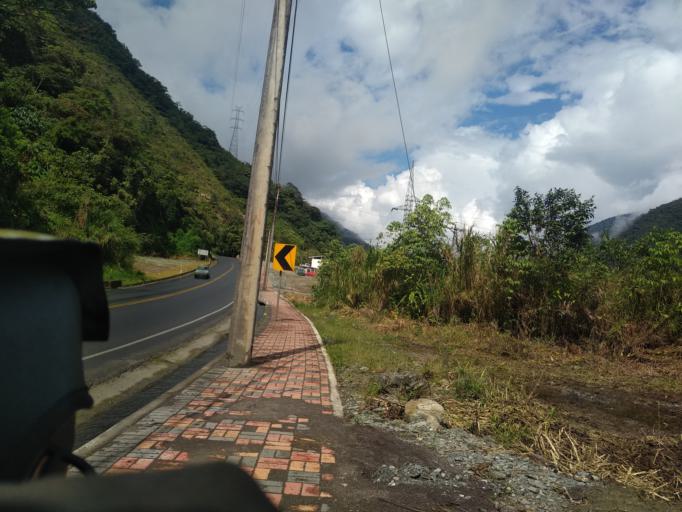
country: EC
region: Tungurahua
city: Banos
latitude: -1.4003
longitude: -78.2924
